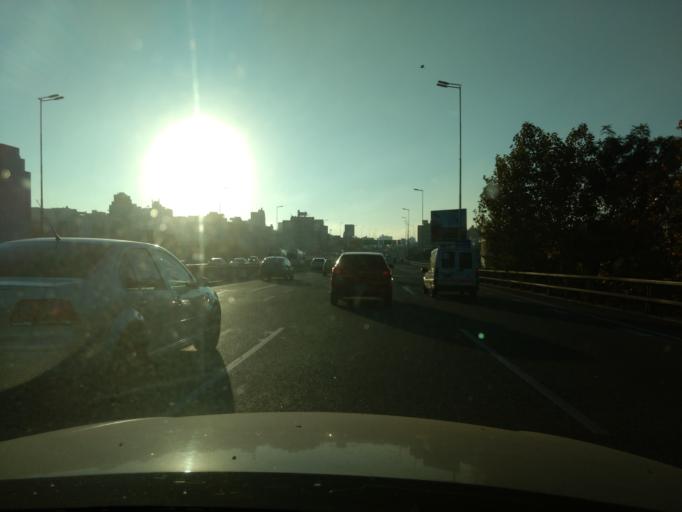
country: AR
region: Buenos Aires F.D.
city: Buenos Aires
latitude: -34.6272
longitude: -58.4133
